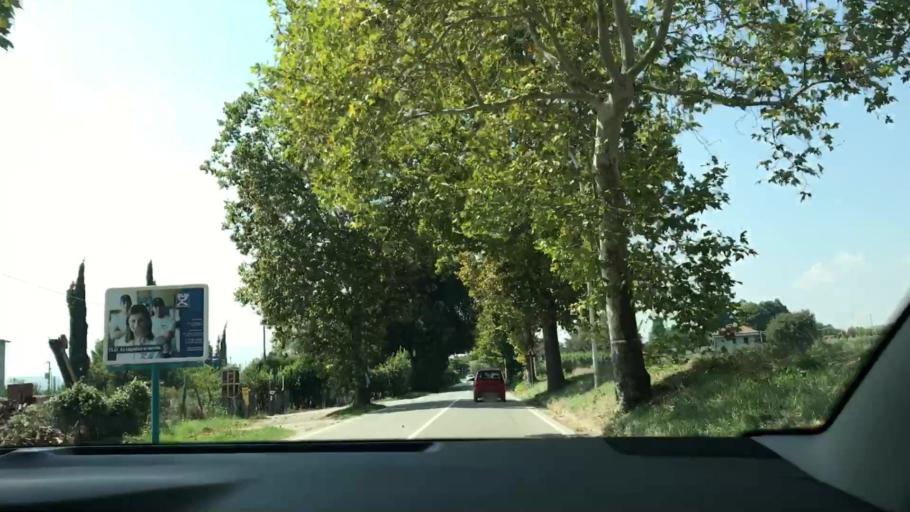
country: IT
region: The Marches
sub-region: Provincia di Ascoli Piceno
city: Centobuchi
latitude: 42.8956
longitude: 13.8421
